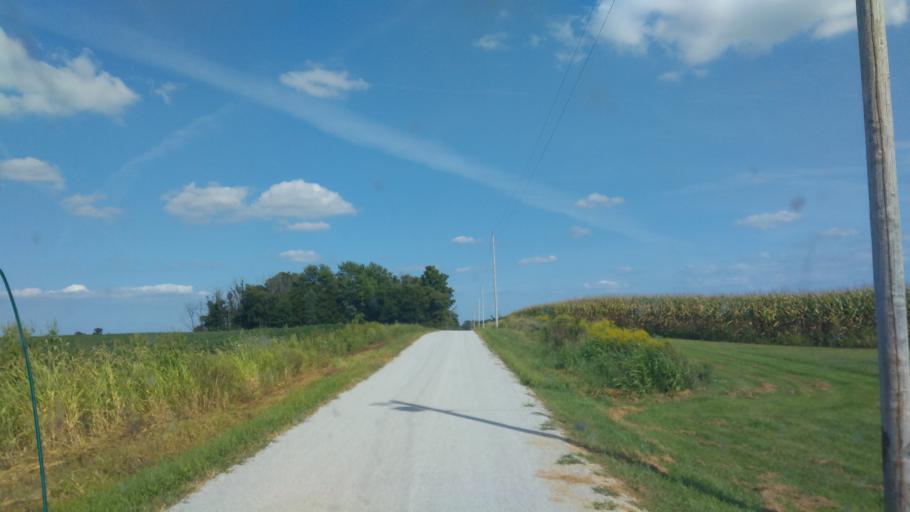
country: US
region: Ohio
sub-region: Hardin County
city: Kenton
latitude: 40.6291
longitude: -83.4564
